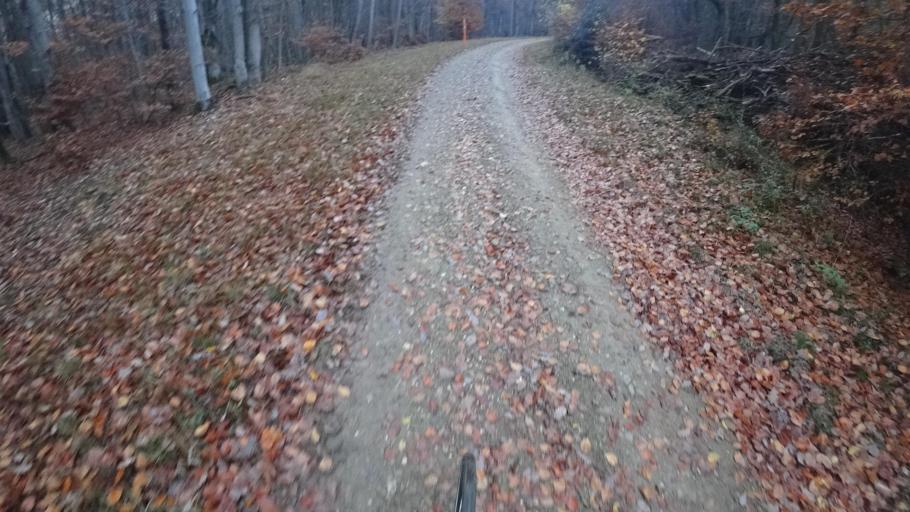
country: DE
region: Rheinland-Pfalz
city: Rech
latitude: 50.5128
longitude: 7.0500
